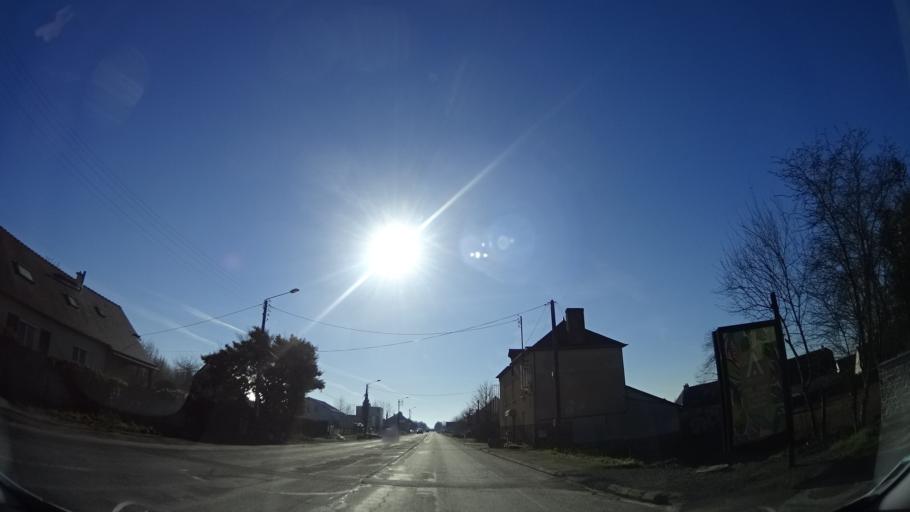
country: FR
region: Brittany
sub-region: Departement d'Ille-et-Vilaine
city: La Meziere
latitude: 48.2174
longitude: -1.7473
